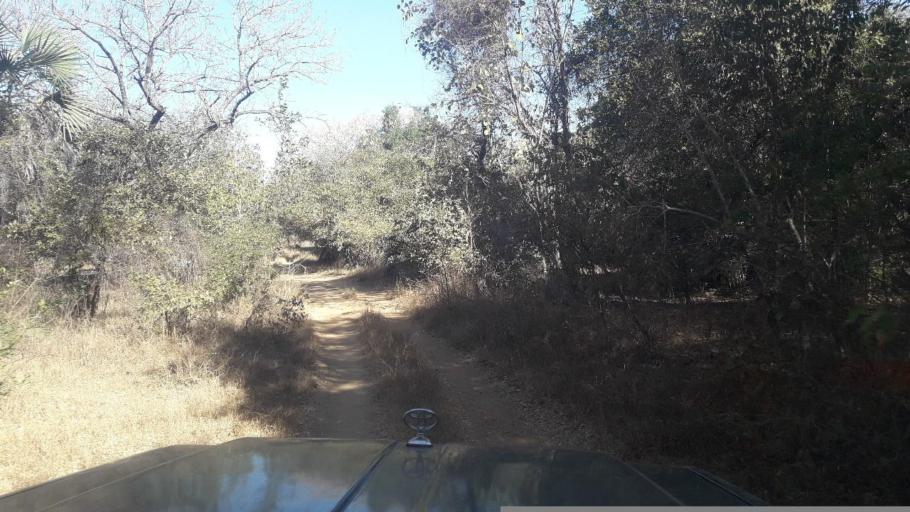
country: MG
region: Boeny
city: Sitampiky
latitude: -16.3988
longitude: 45.5973
